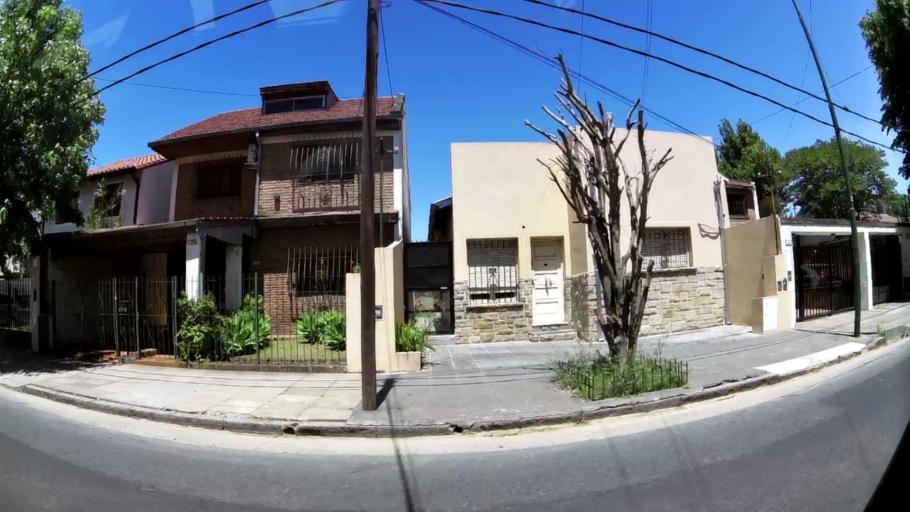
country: AR
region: Buenos Aires
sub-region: Partido de San Isidro
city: San Isidro
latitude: -34.4965
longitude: -58.5153
